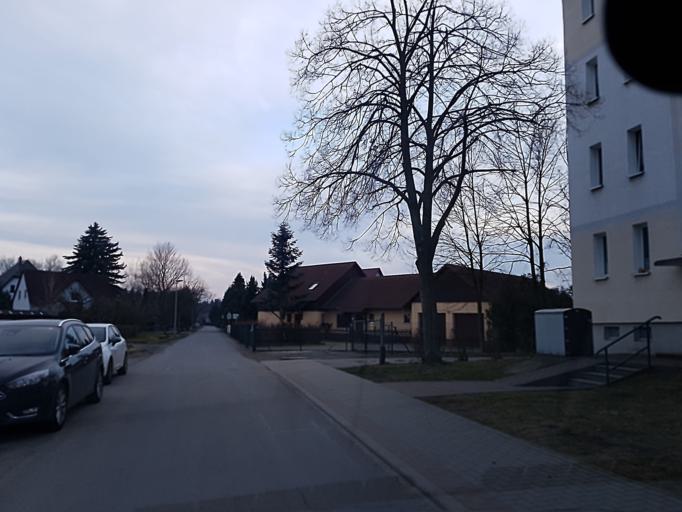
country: DE
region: Brandenburg
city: Doberlug-Kirchhain
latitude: 51.6342
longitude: 13.5663
